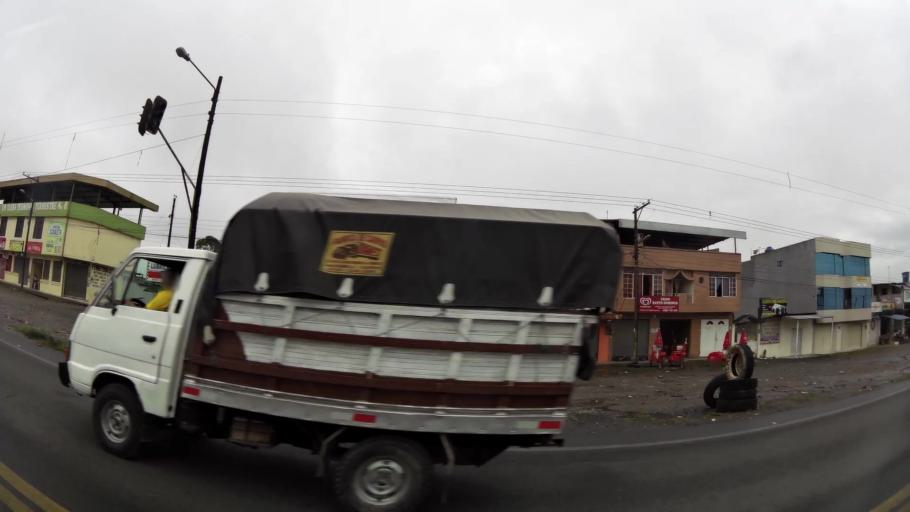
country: EC
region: Santo Domingo de los Tsachilas
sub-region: Canton Santo Domingo de los Colorados
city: Santo Domingo de los Colorados
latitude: -0.2374
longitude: -79.1773
